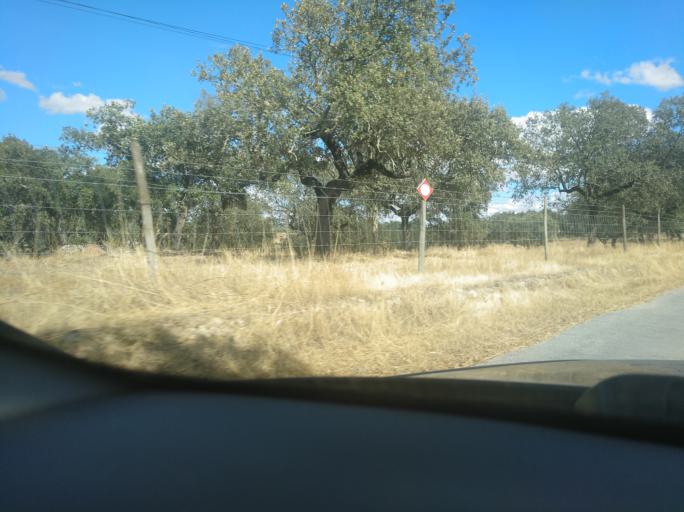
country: ES
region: Extremadura
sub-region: Provincia de Badajoz
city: La Codosera
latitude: 39.1218
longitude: -7.1558
